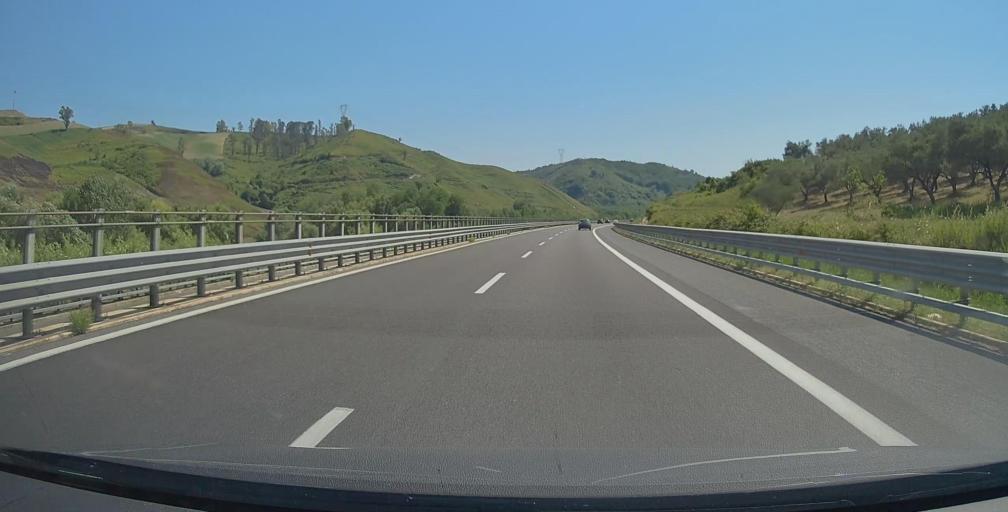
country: IT
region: Calabria
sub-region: Provincia di Vibo-Valentia
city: Francica
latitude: 38.5884
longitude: 16.1358
